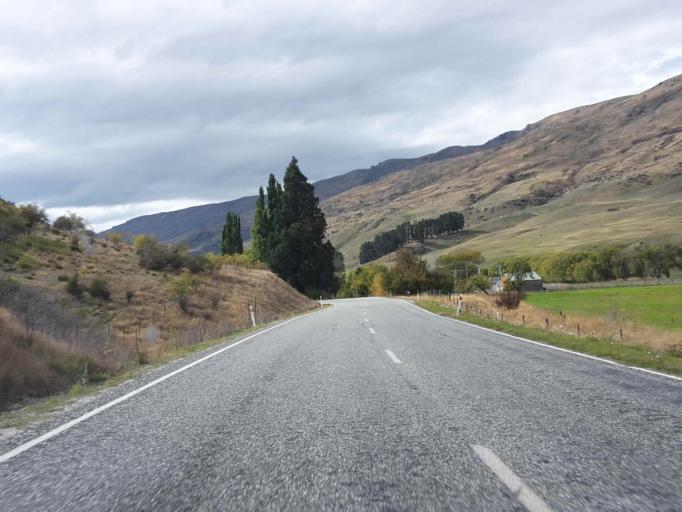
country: NZ
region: Otago
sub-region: Queenstown-Lakes District
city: Wanaka
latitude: -44.8504
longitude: 169.0398
